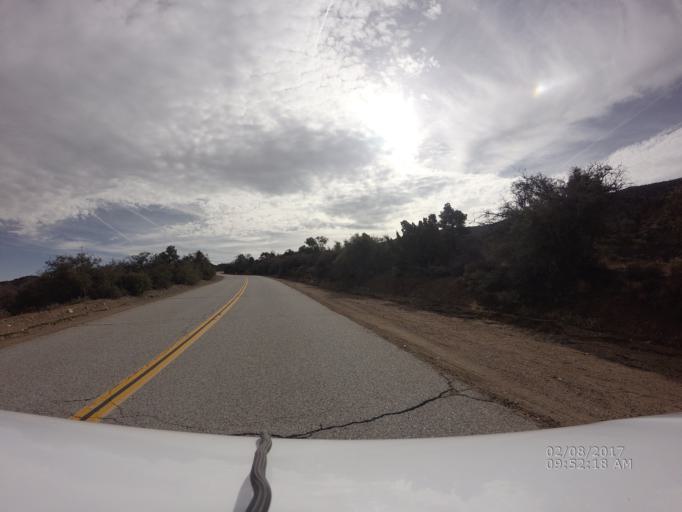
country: US
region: California
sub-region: San Bernardino County
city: Pinon Hills
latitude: 34.4267
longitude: -117.8079
